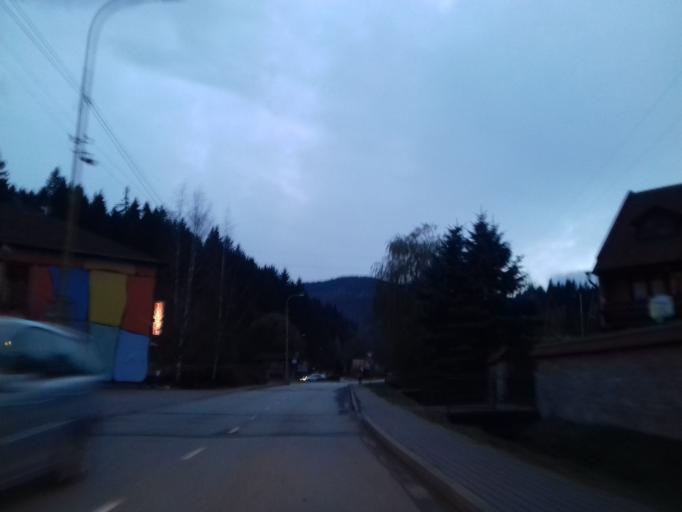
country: SK
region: Zilinsky
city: Ruzomberok
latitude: 49.0820
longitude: 19.2815
